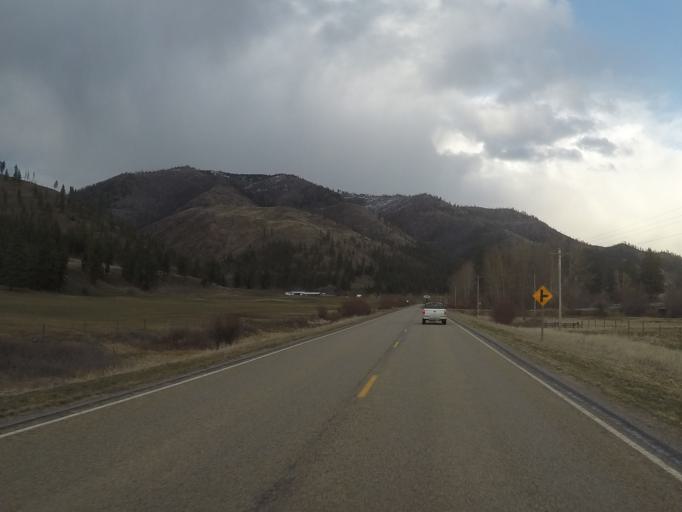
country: US
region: Montana
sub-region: Missoula County
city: Lolo
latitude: 46.7640
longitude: -114.2803
